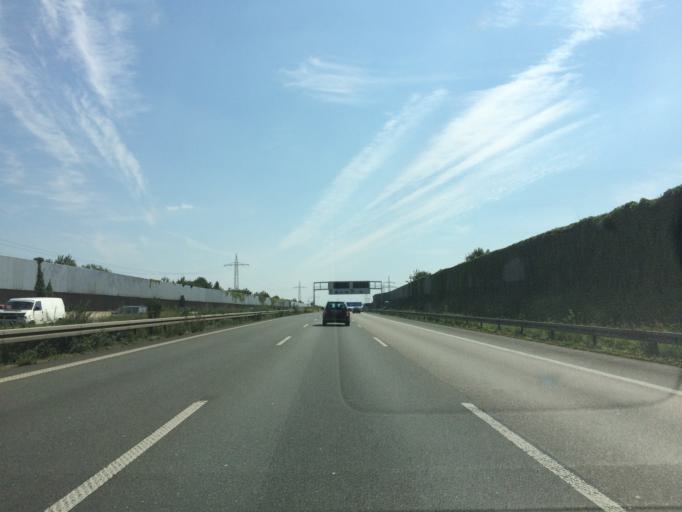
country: DE
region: North Rhine-Westphalia
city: Castrop-Rauxel
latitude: 51.5979
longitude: 7.3365
